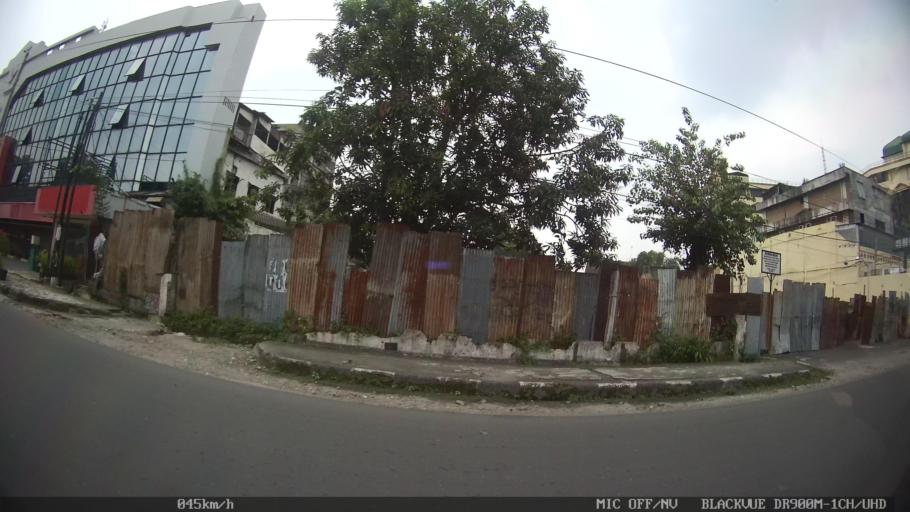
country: ID
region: North Sumatra
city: Medan
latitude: 3.5775
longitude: 98.6870
